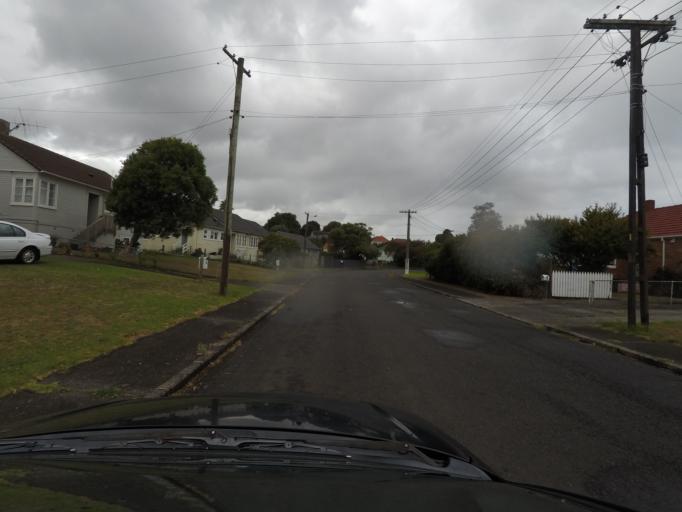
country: NZ
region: Auckland
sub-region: Auckland
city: Rosebank
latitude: -36.8980
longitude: 174.7157
